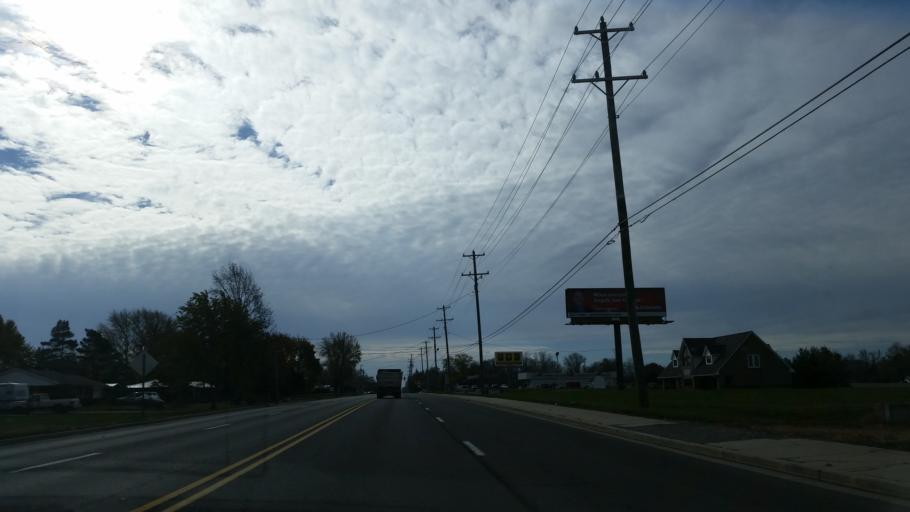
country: US
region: Indiana
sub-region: Howard County
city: Indian Heights
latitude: 40.4428
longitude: -86.1652
